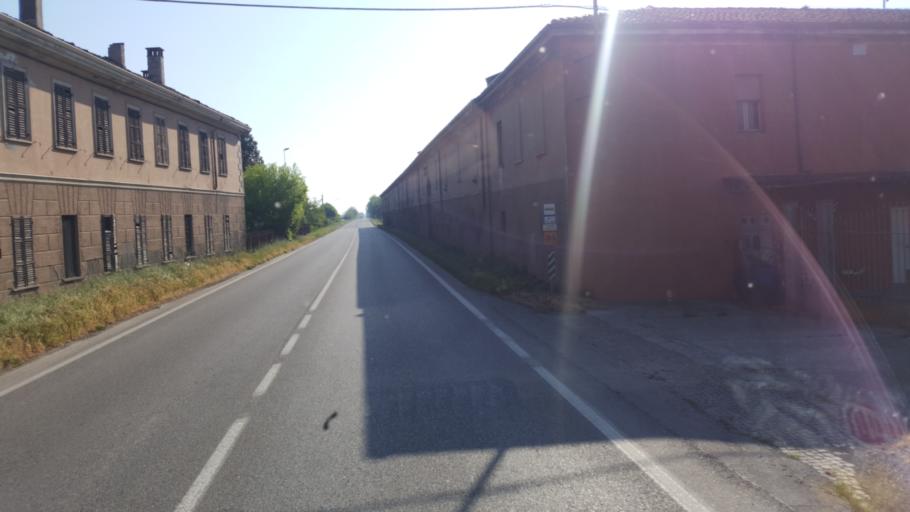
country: IT
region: Lombardy
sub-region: Provincia di Cremona
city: Pessina Cremonese
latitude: 45.1762
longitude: 10.2453
